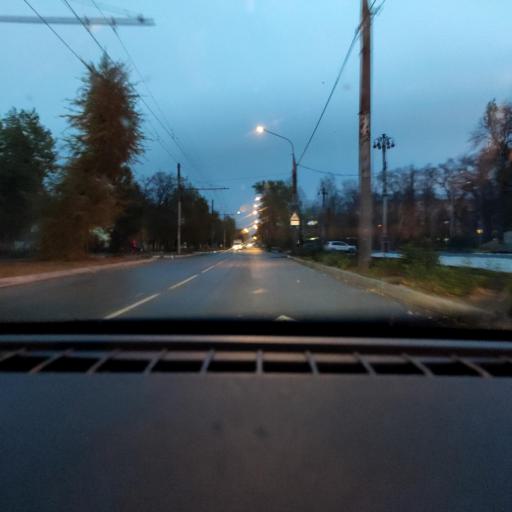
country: RU
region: Voronezj
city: Voronezh
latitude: 51.6382
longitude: 39.2416
